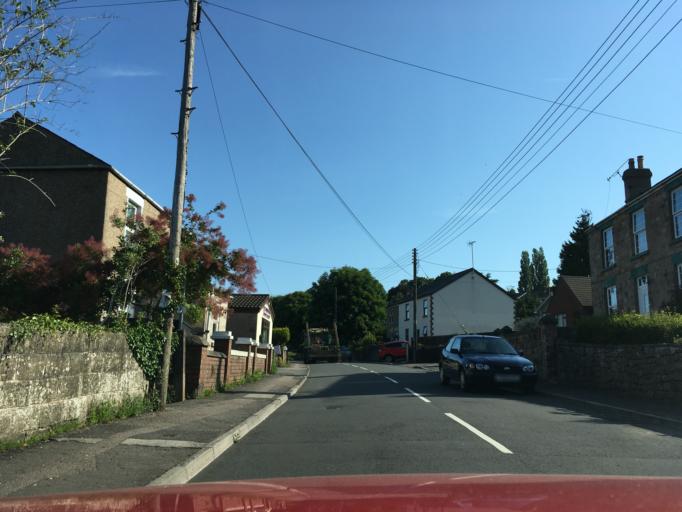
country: GB
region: England
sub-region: Gloucestershire
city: Cinderford
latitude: 51.8095
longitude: -2.5040
